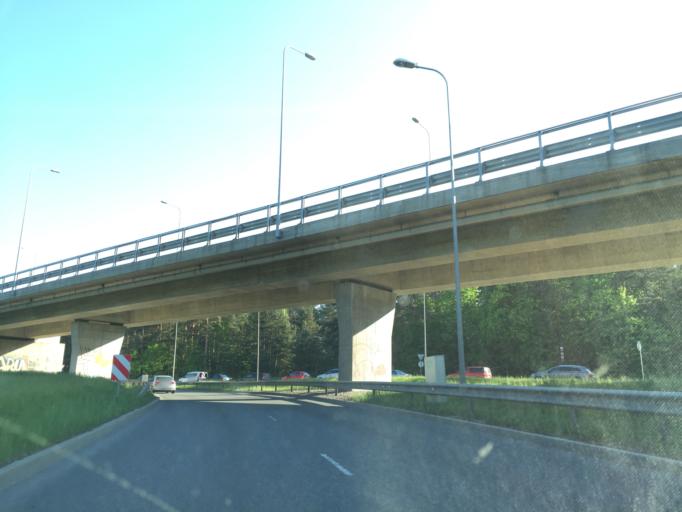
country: LV
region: Kekava
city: Balozi
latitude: 56.9017
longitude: 24.1336
